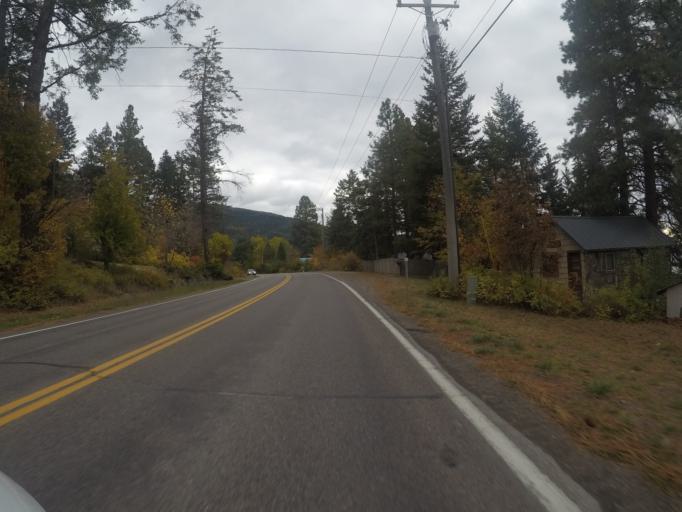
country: US
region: Montana
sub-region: Flathead County
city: Bigfork
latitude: 48.0002
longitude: -114.0497
